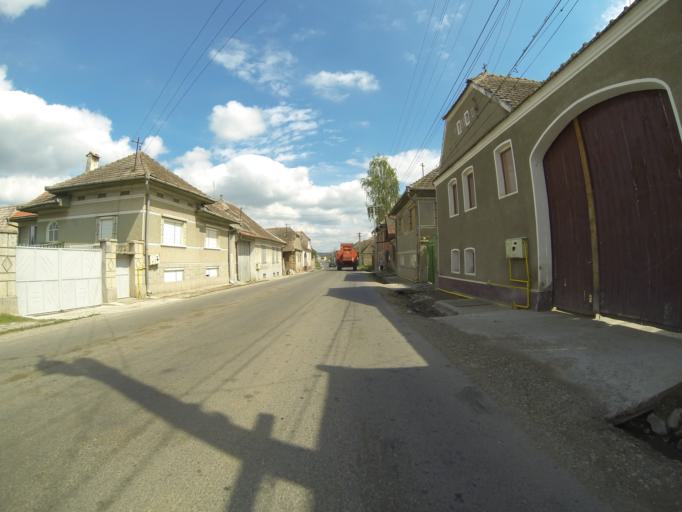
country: RO
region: Brasov
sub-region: Comuna Hoghiz
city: Hoghiz
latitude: 45.9661
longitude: 25.2986
